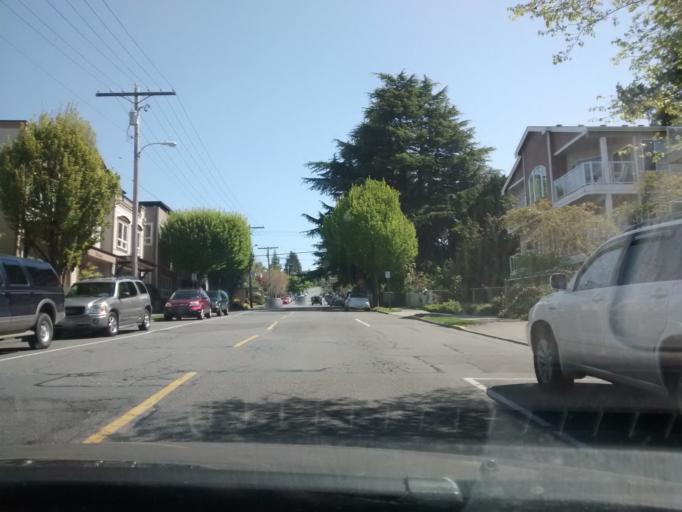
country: US
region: Washington
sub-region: Snohomish County
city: Edmonds
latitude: 47.8097
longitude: -122.3760
